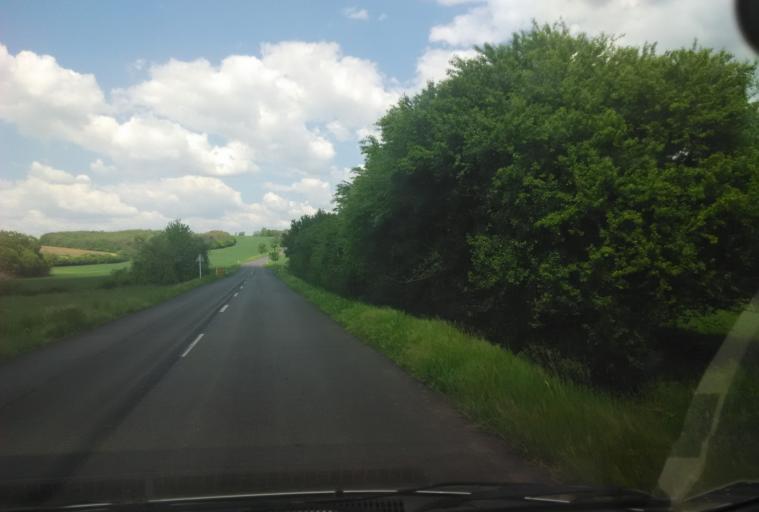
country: SK
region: Banskobystricky
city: Dudince
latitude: 48.2085
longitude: 18.7899
